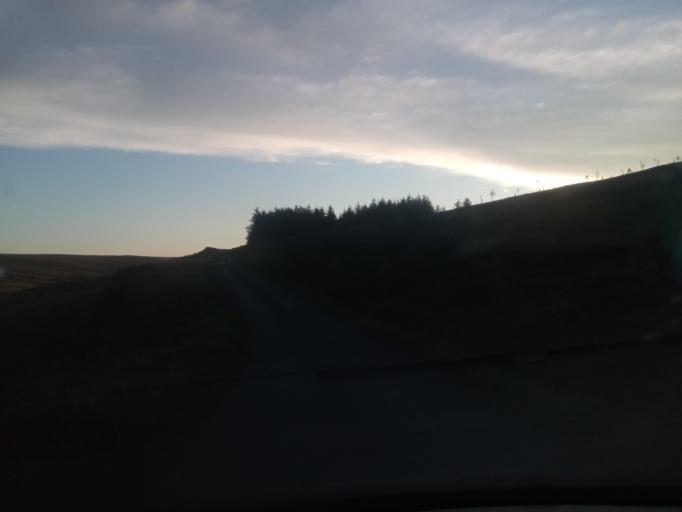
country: GB
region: England
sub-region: Northumberland
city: Bardon Mill
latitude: 54.7987
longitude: -2.3472
